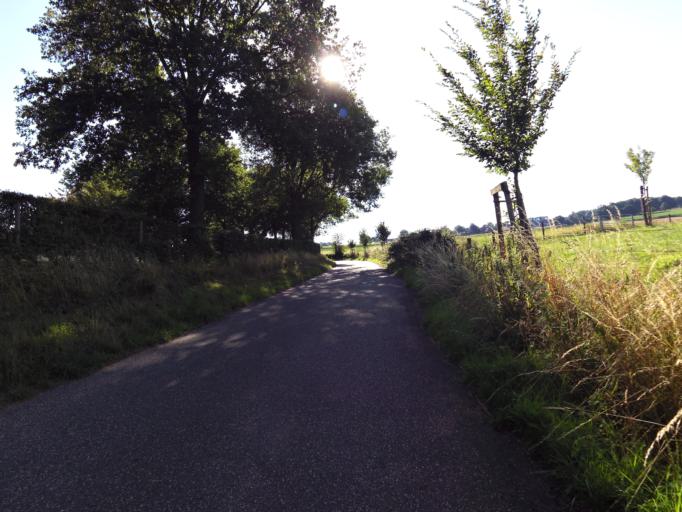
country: BE
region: Wallonia
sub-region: Province de Liege
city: Plombieres
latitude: 50.7896
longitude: 5.9307
